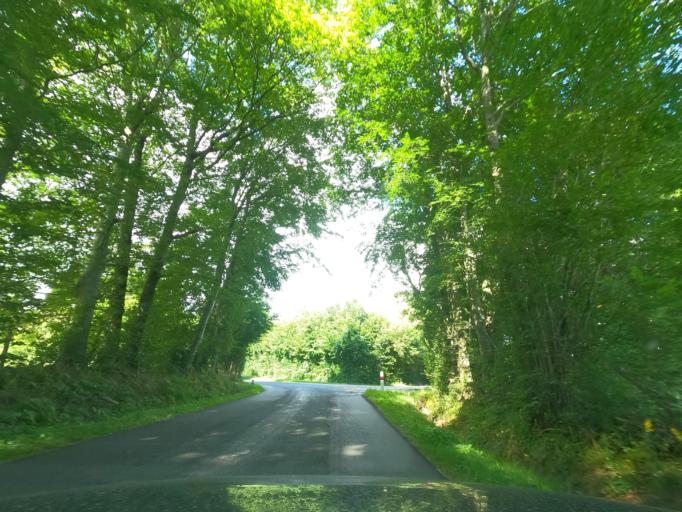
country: FR
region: Lower Normandy
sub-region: Departement de l'Orne
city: Gace
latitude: 48.7830
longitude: 0.2603
